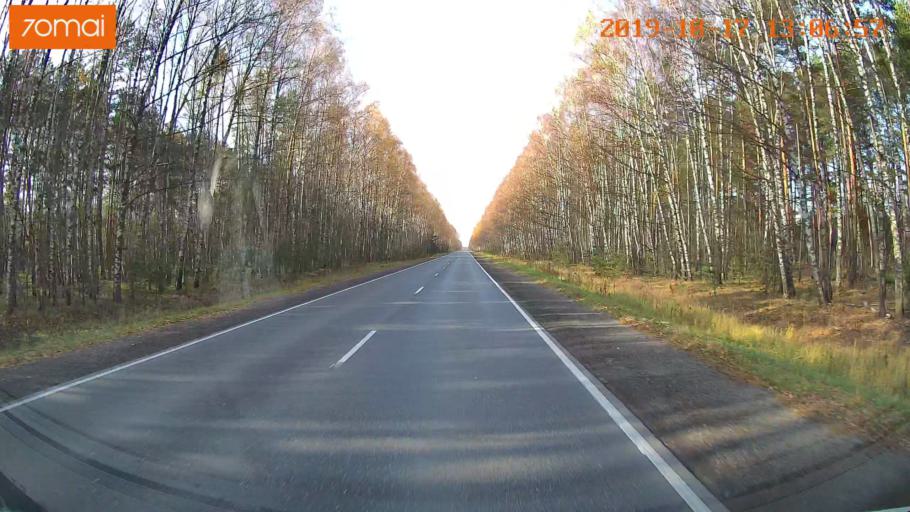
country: RU
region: Rjazan
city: Syntul
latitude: 54.9787
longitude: 41.3021
